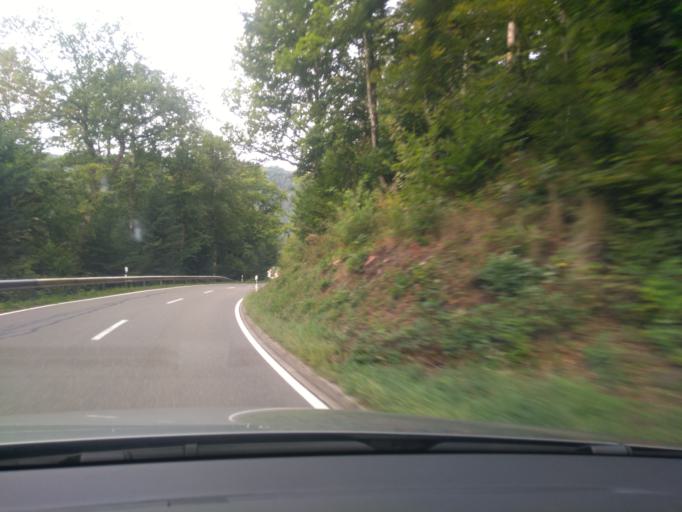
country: DE
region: Baden-Wuerttemberg
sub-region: Karlsruhe Region
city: Hofen an der Enz
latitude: 48.8021
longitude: 8.5981
